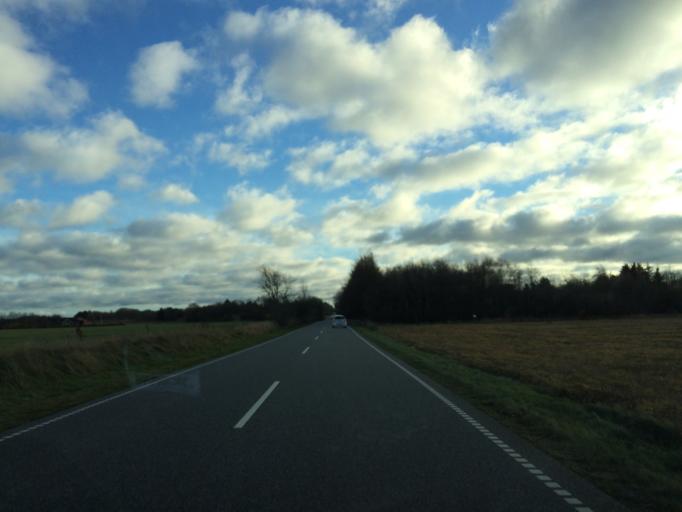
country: DK
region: Central Jutland
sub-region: Herning Kommune
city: Kibaek
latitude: 55.9358
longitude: 8.8941
